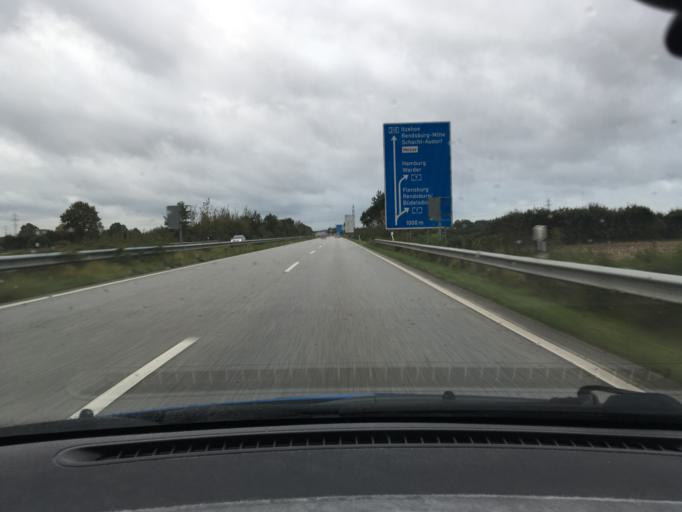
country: DE
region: Schleswig-Holstein
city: Hassmoor
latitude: 54.3108
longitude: 9.7795
